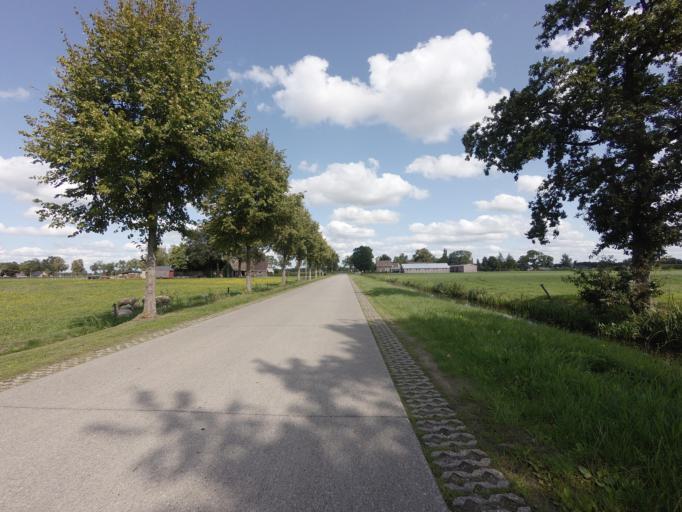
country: NL
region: Overijssel
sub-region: Gemeente Staphorst
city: Staphorst
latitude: 52.6057
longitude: 6.2548
